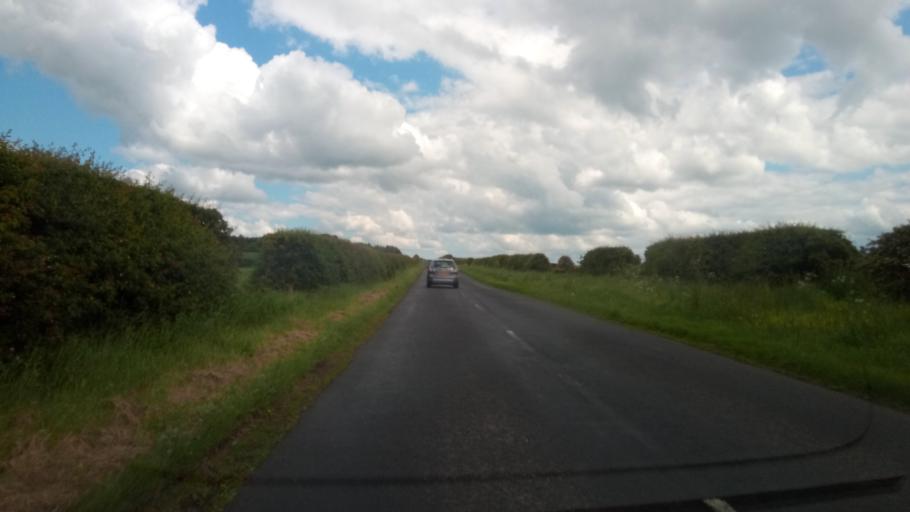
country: GB
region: Scotland
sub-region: The Scottish Borders
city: Kelso
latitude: 55.5903
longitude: -2.3685
